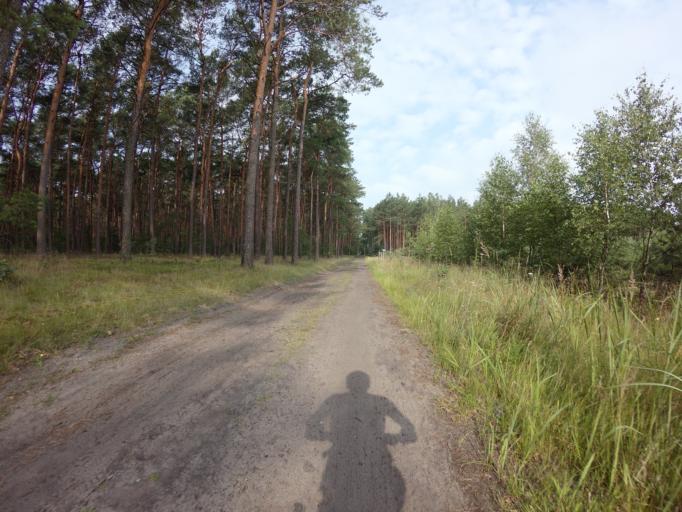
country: PL
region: Kujawsko-Pomorskie
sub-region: Powiat bydgoski
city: Osielsko
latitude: 53.1452
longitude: 18.0622
